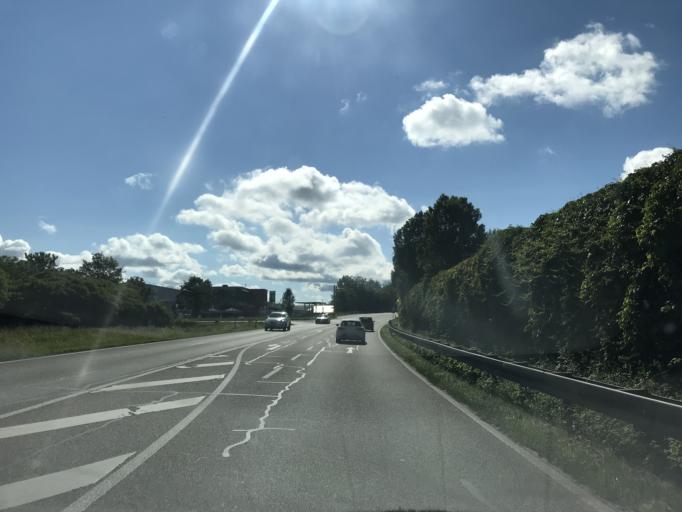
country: DE
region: Baden-Wuerttemberg
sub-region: Freiburg Region
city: Steinen
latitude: 47.6404
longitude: 7.7034
